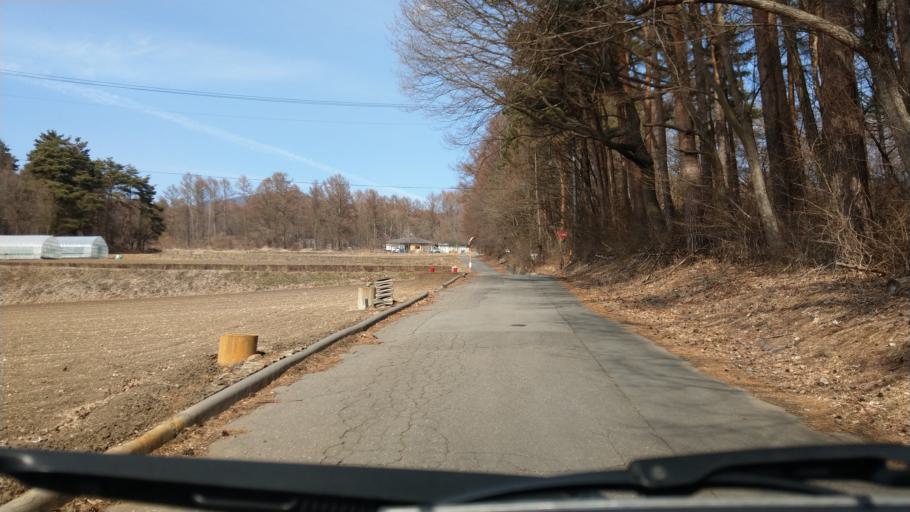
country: JP
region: Nagano
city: Komoro
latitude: 36.3397
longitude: 138.4638
